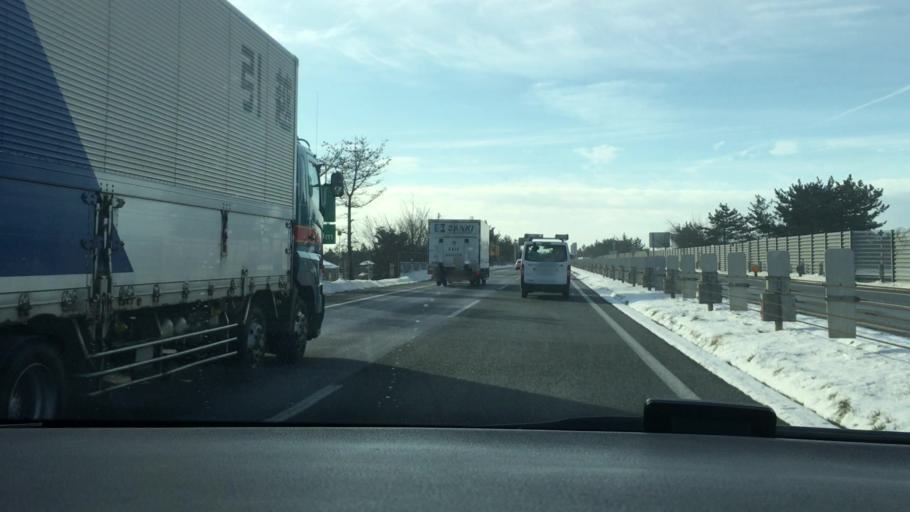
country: JP
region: Iwate
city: Hanamaki
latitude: 39.3939
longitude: 141.0923
